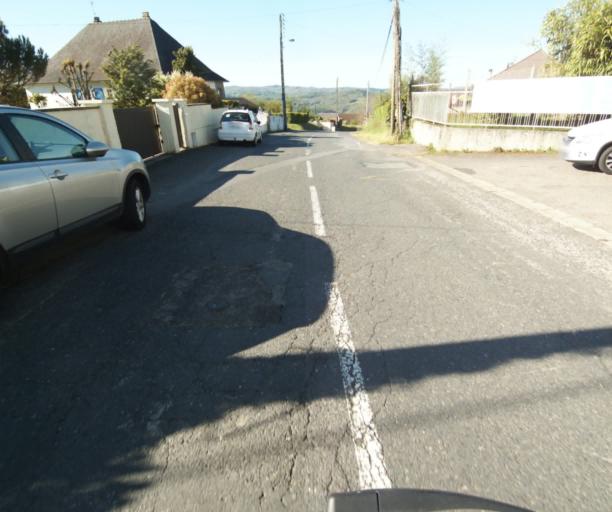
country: FR
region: Limousin
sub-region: Departement de la Correze
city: Tulle
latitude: 45.2675
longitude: 1.7856
